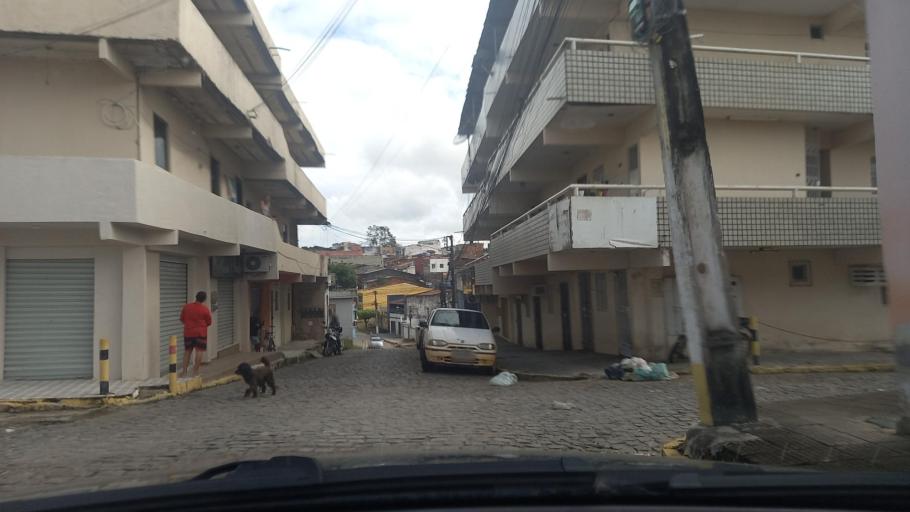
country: BR
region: Pernambuco
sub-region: Vitoria De Santo Antao
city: Vitoria de Santo Antao
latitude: -8.1111
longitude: -35.2963
